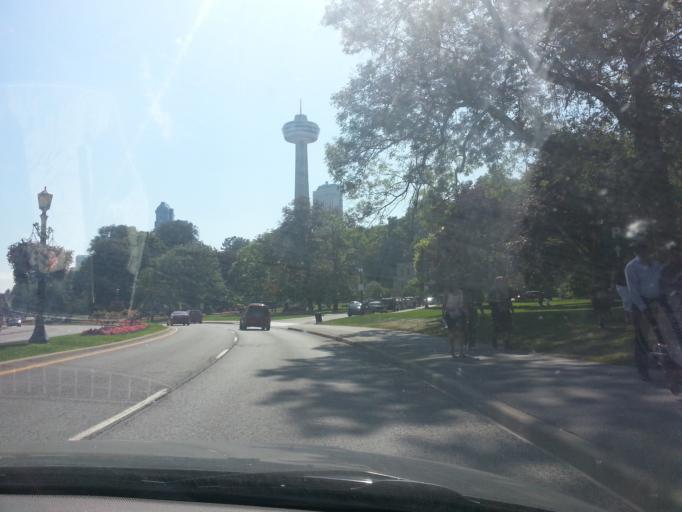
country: CA
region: Ontario
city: Niagara Falls
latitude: 43.0880
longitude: -79.0753
